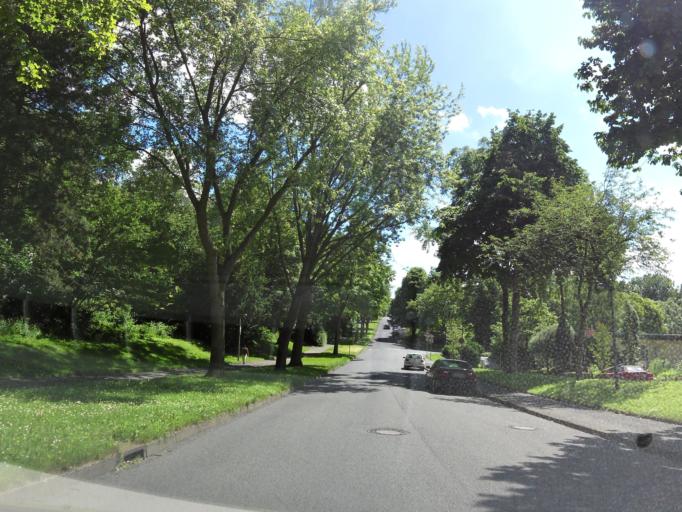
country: DE
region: Lower Saxony
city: Goettingen
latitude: 51.5146
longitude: 9.9715
